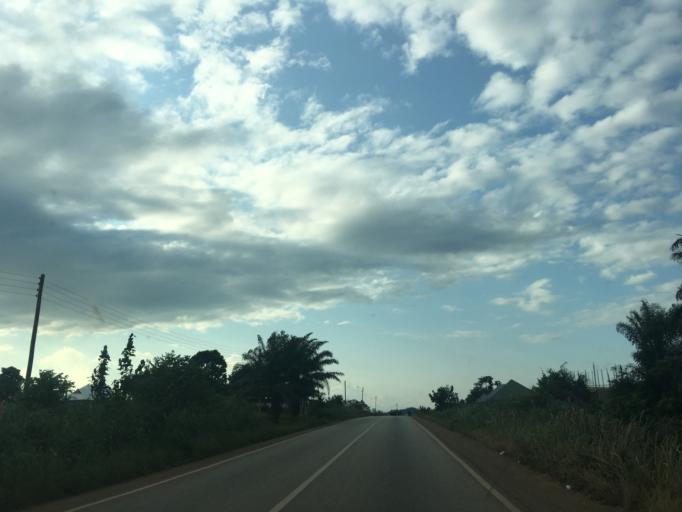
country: GH
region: Western
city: Bibiani
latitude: 6.4283
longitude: -2.3061
